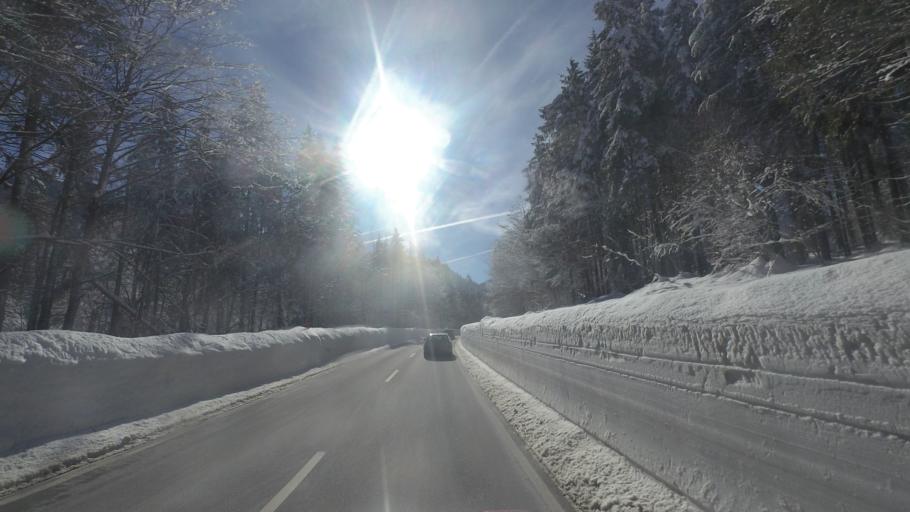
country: DE
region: Bavaria
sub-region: Upper Bavaria
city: Reit im Winkl
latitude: 47.6747
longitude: 12.5467
